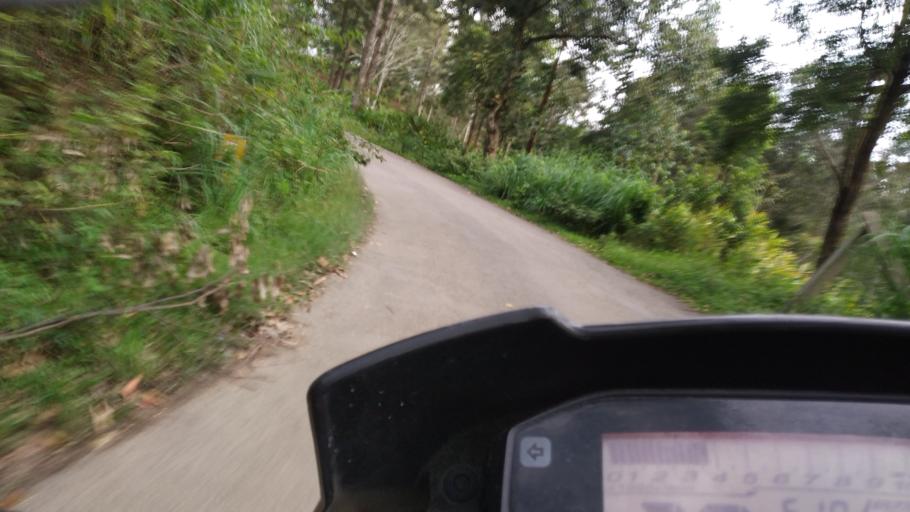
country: IN
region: Tamil Nadu
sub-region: Theni
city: Bodinayakkanur
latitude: 10.0261
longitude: 77.2314
